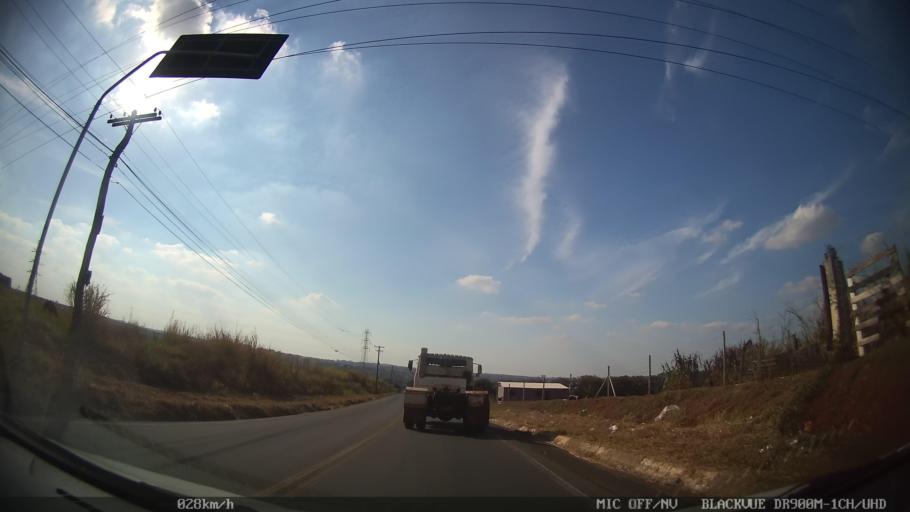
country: BR
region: Sao Paulo
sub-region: Hortolandia
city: Hortolandia
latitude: -22.8420
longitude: -47.2070
